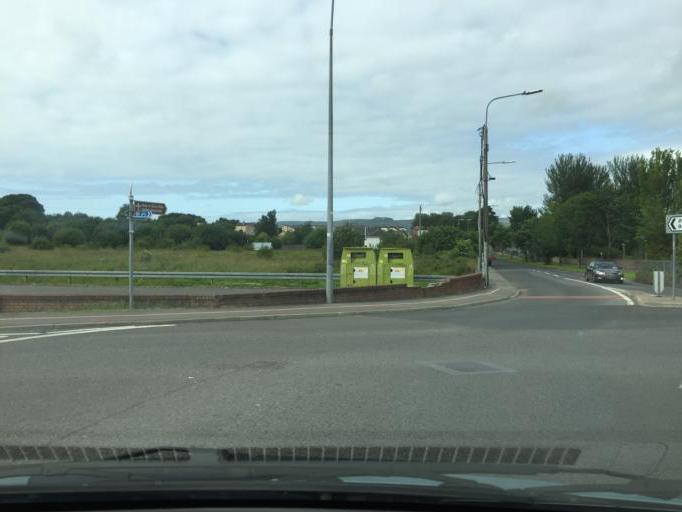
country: IE
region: Connaught
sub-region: Sligo
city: Sligo
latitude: 54.2776
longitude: -8.4715
